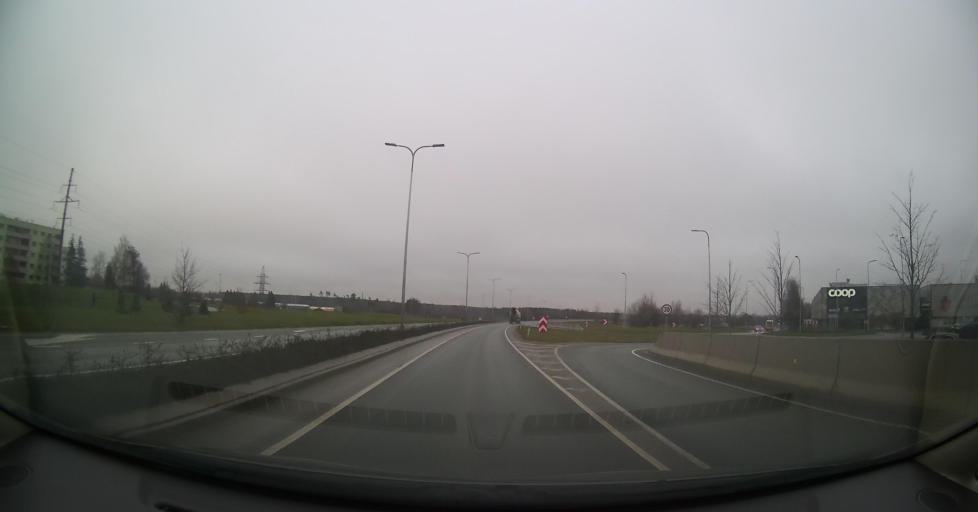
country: EE
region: Tartu
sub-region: Tartu linn
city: Tartu
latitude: 58.3732
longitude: 26.7816
